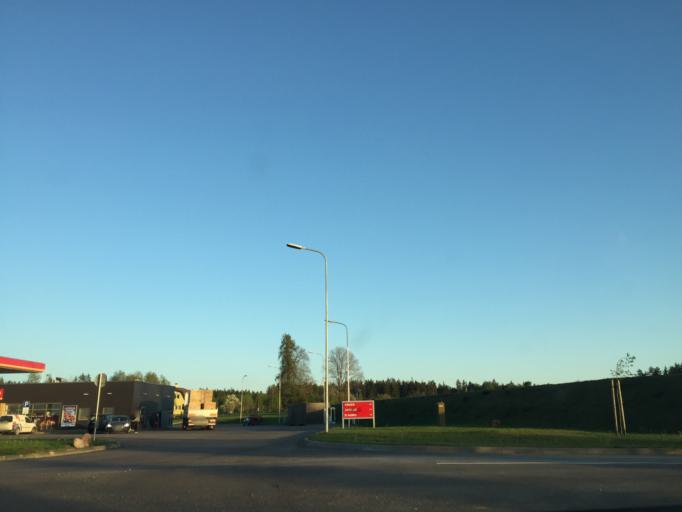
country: LV
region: Ogre
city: Ogre
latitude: 56.8584
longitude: 24.5628
